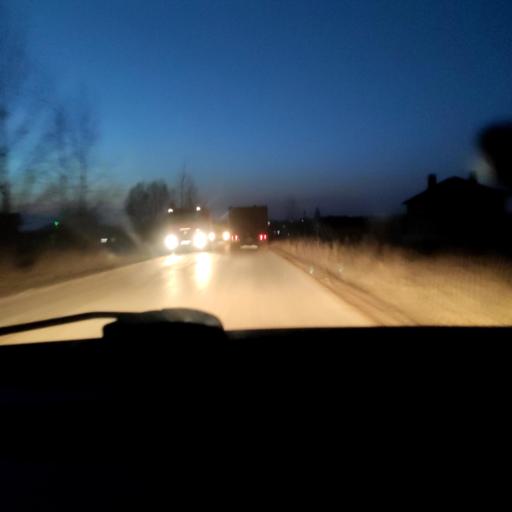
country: RU
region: Bashkortostan
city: Ufa
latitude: 54.7054
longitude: 56.1114
